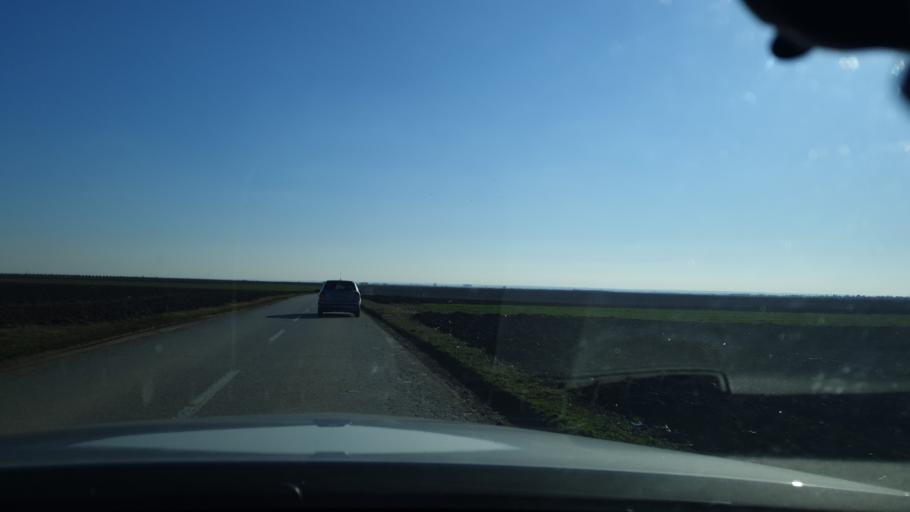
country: RS
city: Vrdnik
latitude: 45.0693
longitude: 19.8090
